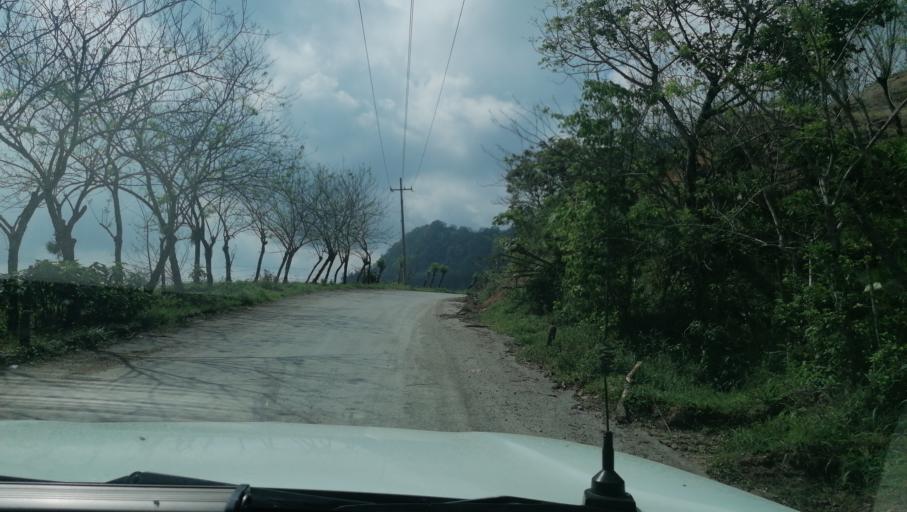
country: MX
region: Chiapas
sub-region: Ocotepec
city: San Pablo Huacano
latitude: 17.2522
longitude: -93.2706
